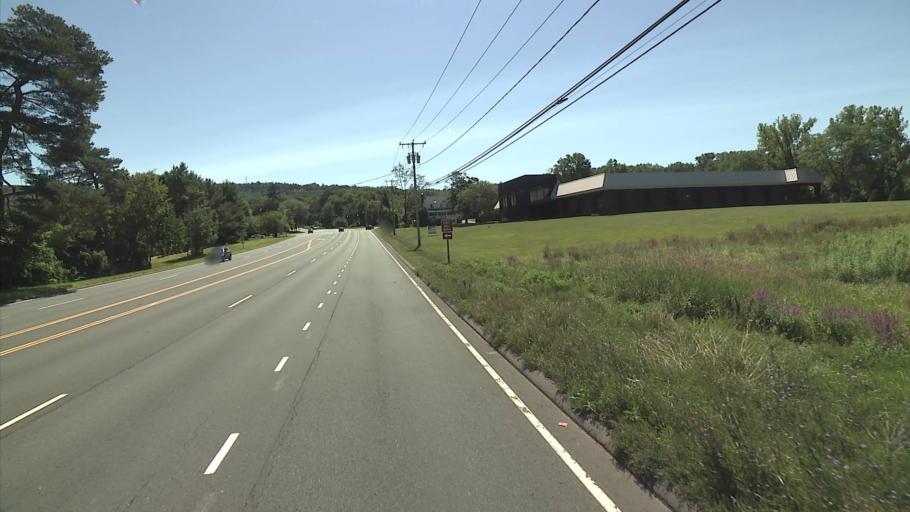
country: US
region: Connecticut
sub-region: Hartford County
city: Weatogue
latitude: 41.8057
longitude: -72.8196
